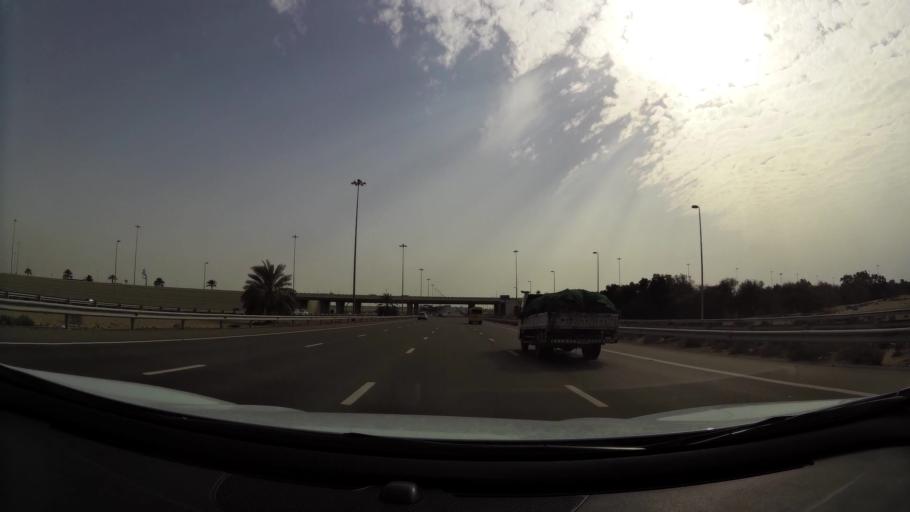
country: AE
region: Abu Dhabi
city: Abu Dhabi
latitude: 24.4114
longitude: 54.6736
